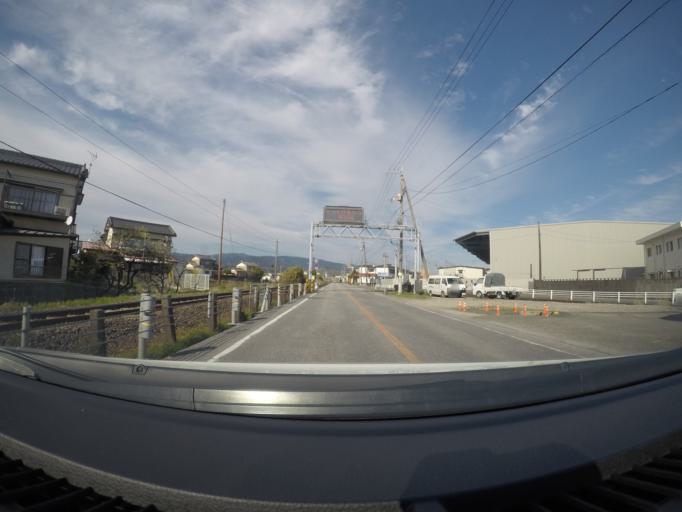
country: JP
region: Kochi
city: Kochi-shi
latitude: 33.5987
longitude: 133.6706
